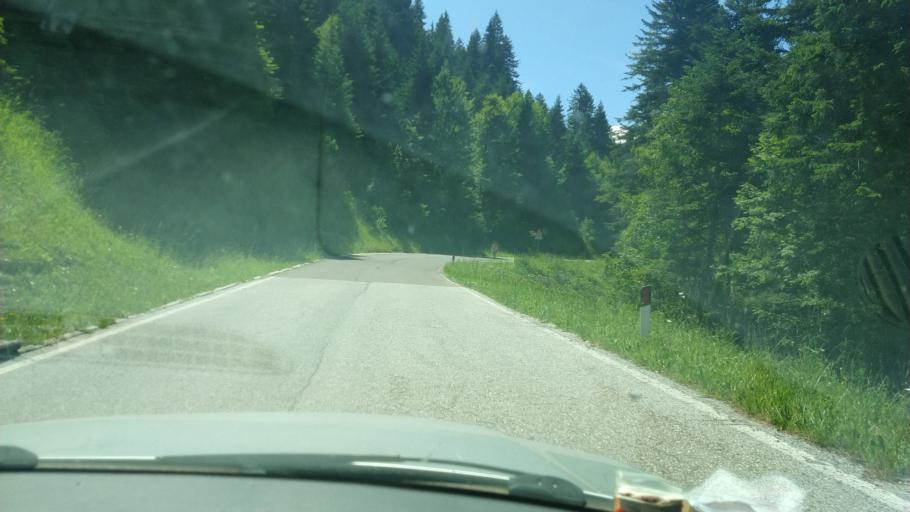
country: IT
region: Trentino-Alto Adige
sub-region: Provincia di Trento
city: Folgaria
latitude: 45.9005
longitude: 11.2105
